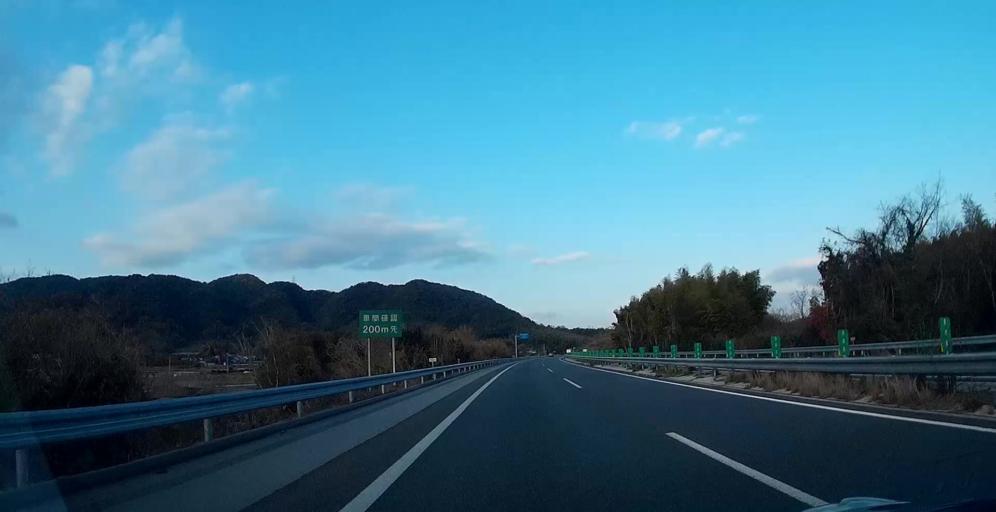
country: JP
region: Kumamoto
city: Uto
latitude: 32.6705
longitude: 130.7148
